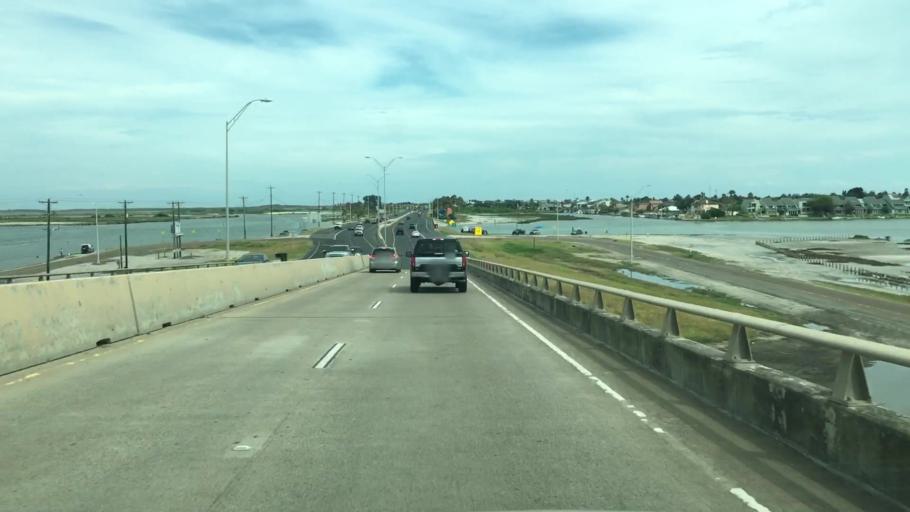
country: US
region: Texas
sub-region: Nueces County
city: Corpus Christi
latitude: 27.6330
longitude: -97.2359
